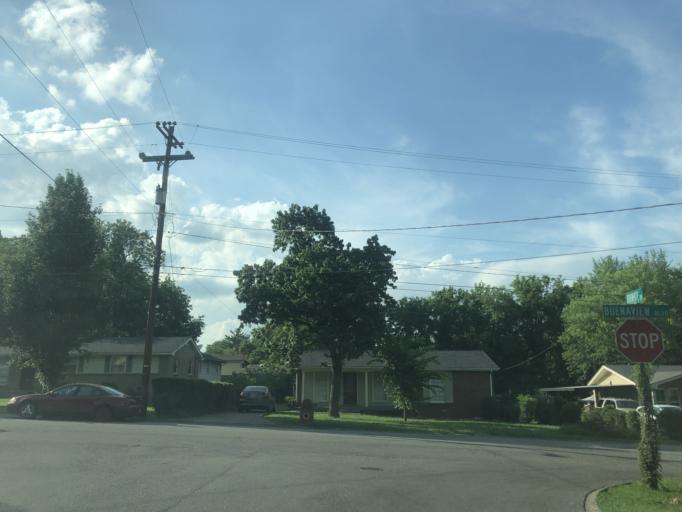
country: US
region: Tennessee
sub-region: Davidson County
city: Nashville
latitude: 36.2275
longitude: -86.8285
